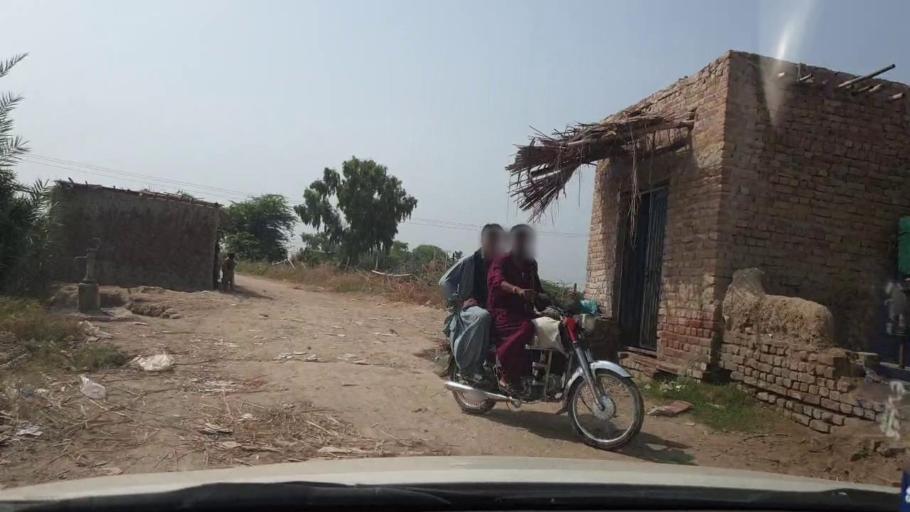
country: PK
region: Sindh
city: Shikarpur
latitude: 27.9745
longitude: 68.6769
